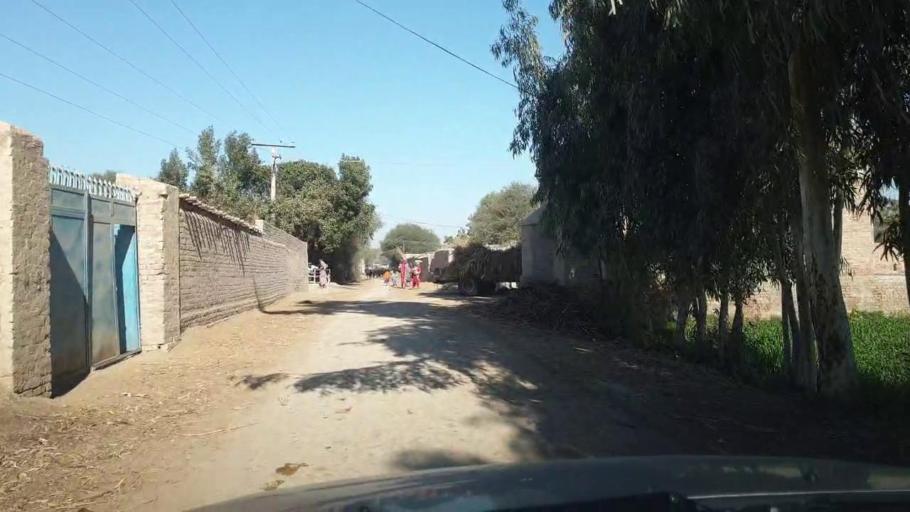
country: PK
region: Sindh
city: Ghotki
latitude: 28.0987
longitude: 69.3423
